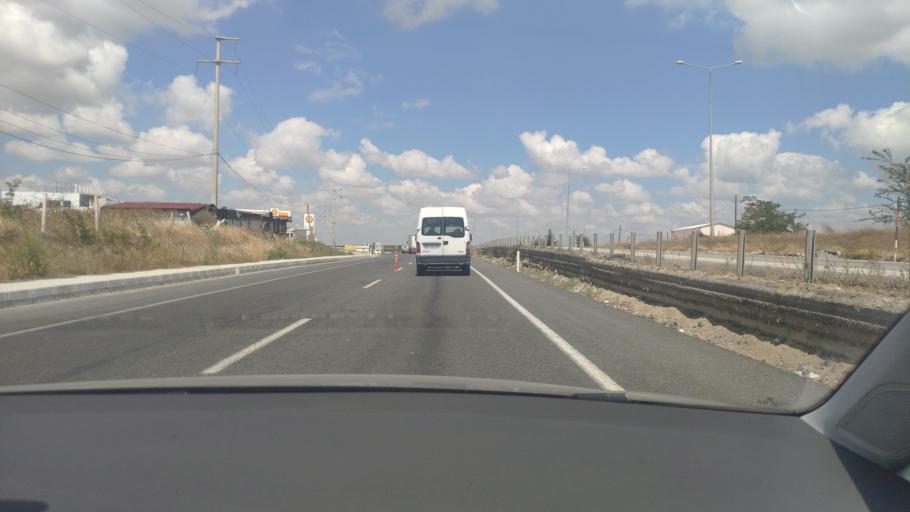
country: TR
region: Tekirdag
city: Sultankoy
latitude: 41.0986
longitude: 27.9508
